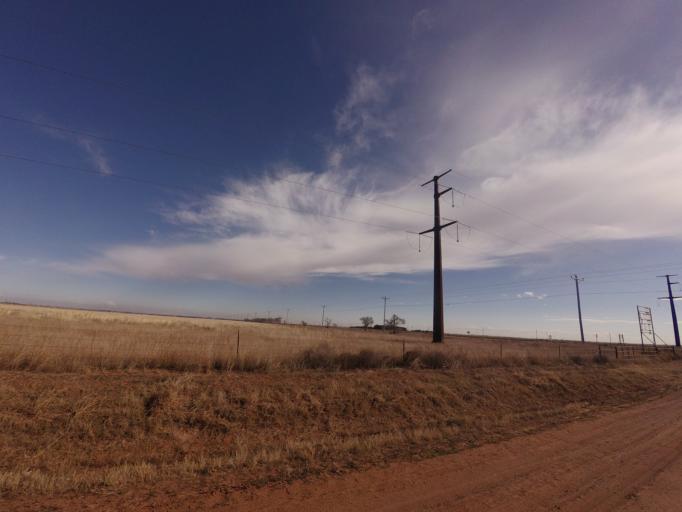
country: US
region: New Mexico
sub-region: Curry County
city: Texico
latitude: 34.3936
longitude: -103.1258
